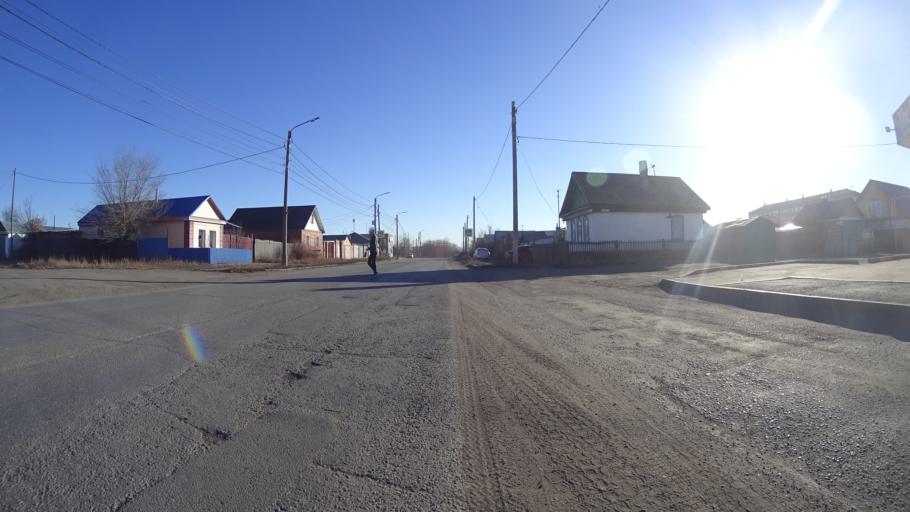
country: RU
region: Chelyabinsk
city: Troitsk
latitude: 54.1056
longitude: 61.5616
